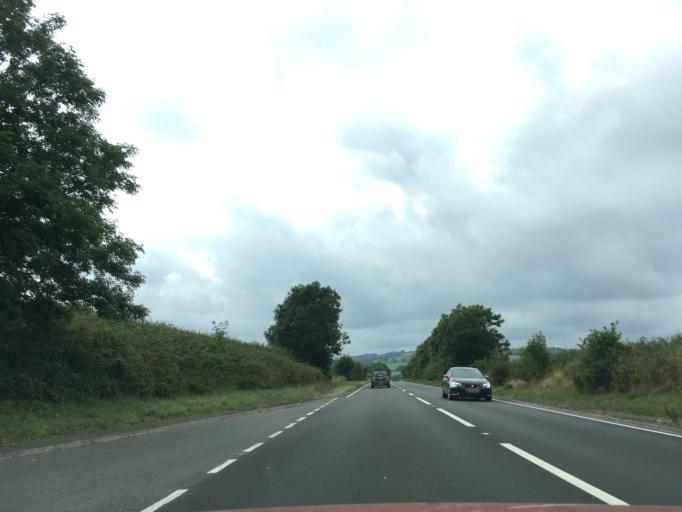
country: GB
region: Wales
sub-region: Carmarthenshire
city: Llanddowror
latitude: 51.8243
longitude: -4.5435
